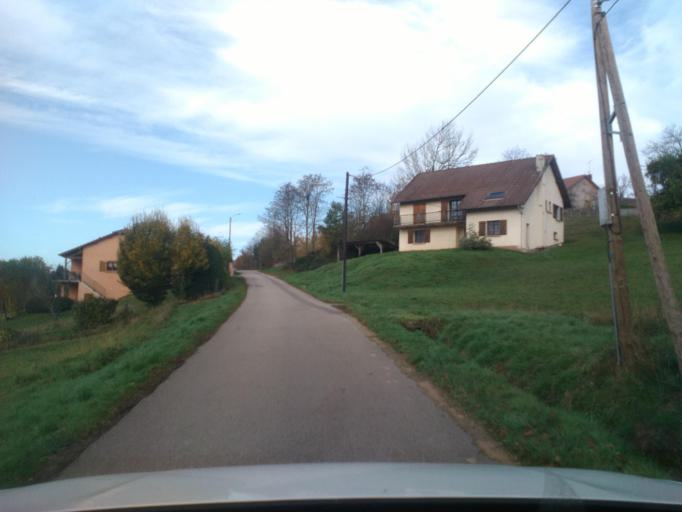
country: FR
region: Lorraine
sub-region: Departement des Vosges
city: Moyenmoutier
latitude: 48.3668
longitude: 6.9325
